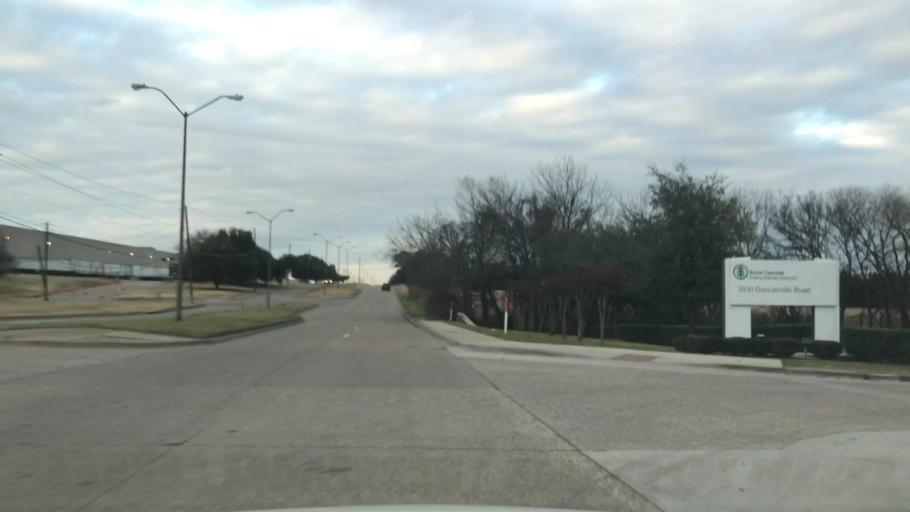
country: US
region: Texas
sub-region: Dallas County
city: Duncanville
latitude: 32.6946
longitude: -96.9085
